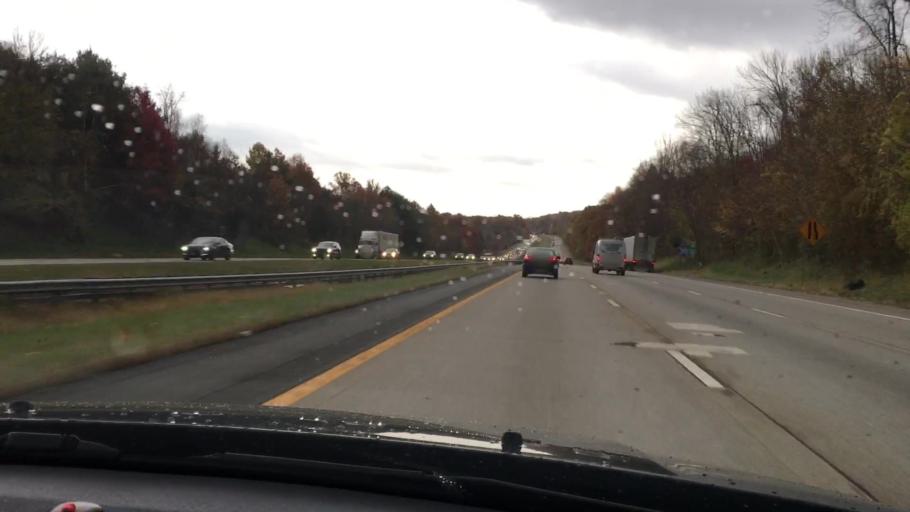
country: US
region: New Jersey
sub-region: Bergen County
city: Franklin Lakes
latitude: 41.0557
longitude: -74.1871
